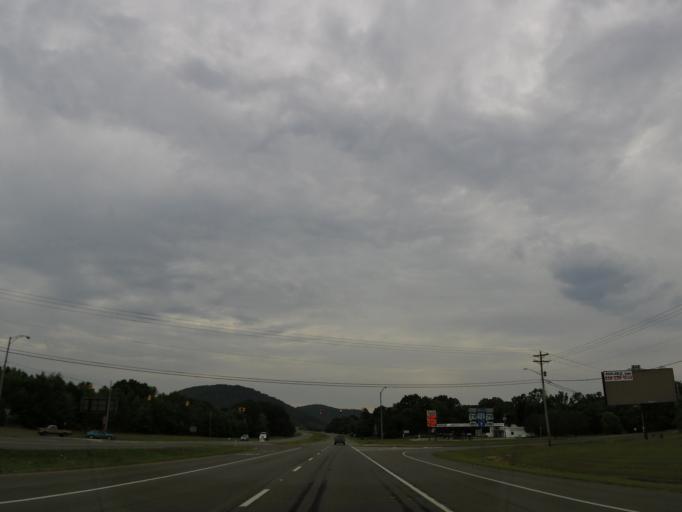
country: US
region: Alabama
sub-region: Jackson County
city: Scottsboro
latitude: 34.6217
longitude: -86.0958
